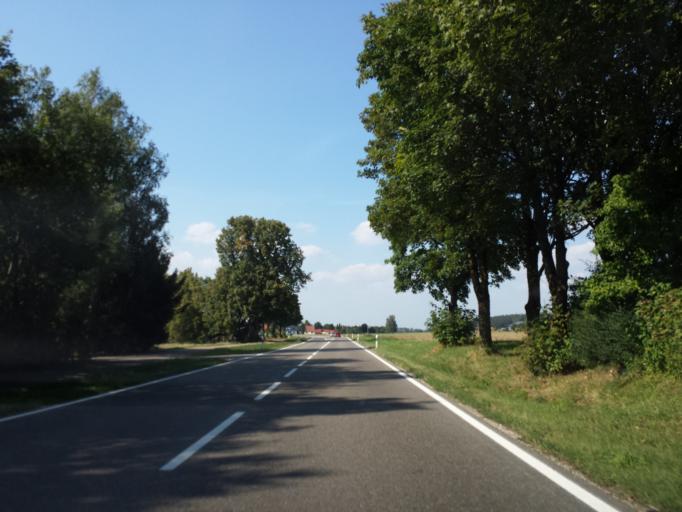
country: DE
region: Bavaria
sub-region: Swabia
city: Deisenhausen
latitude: 48.2785
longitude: 10.3373
